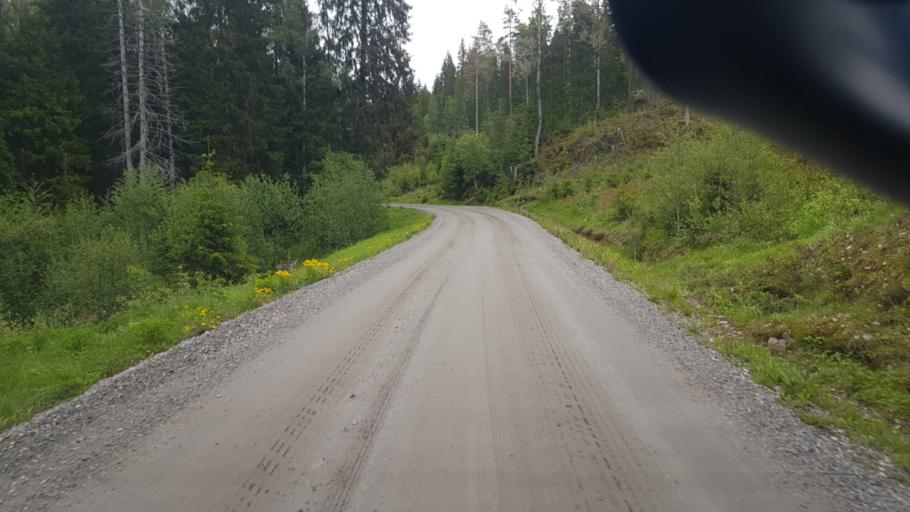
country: NO
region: Ostfold
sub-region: Romskog
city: Romskog
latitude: 59.7130
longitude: 11.9761
